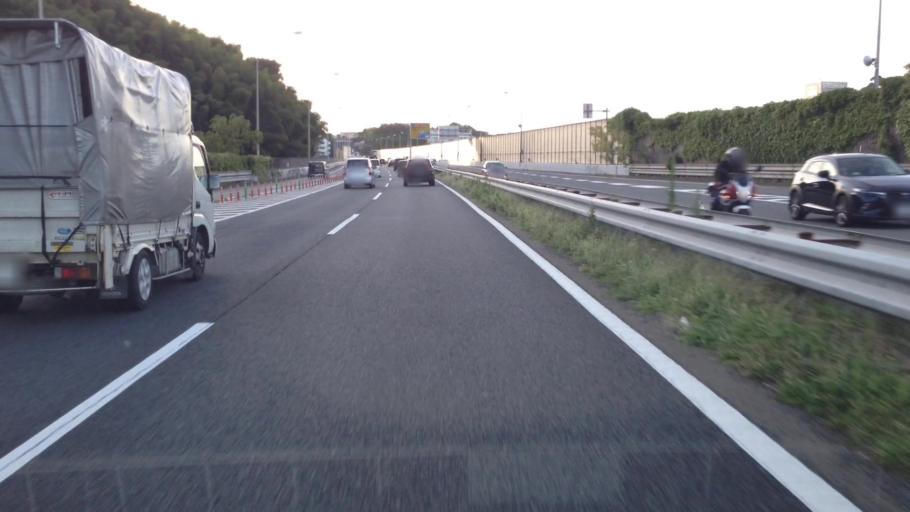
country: JP
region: Kanagawa
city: Kamakura
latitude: 35.3835
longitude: 139.5831
